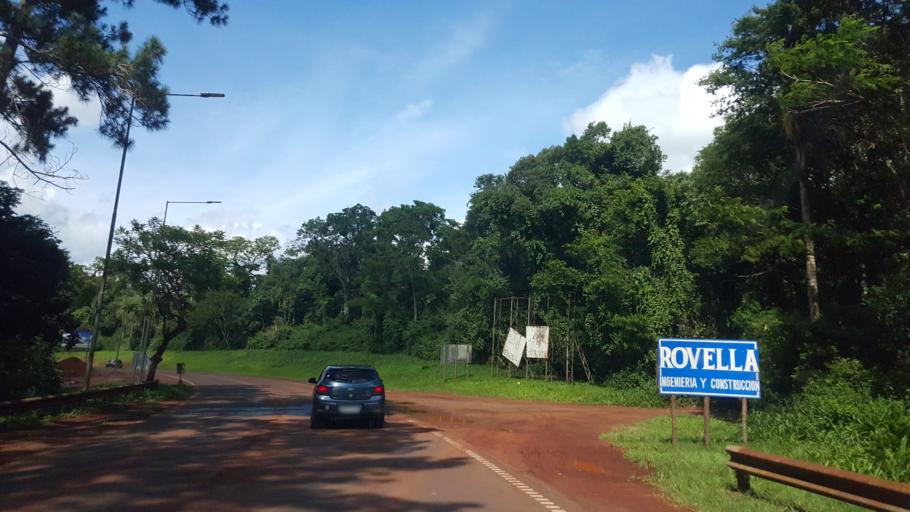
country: AR
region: Misiones
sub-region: Departamento de Iguazu
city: Puerto Iguazu
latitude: -25.7319
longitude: -54.4716
